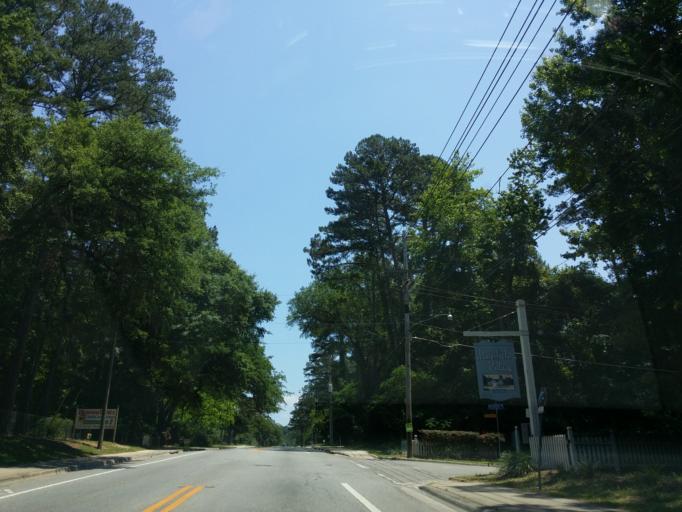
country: US
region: Florida
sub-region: Leon County
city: Tallahassee
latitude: 30.4738
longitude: -84.3295
